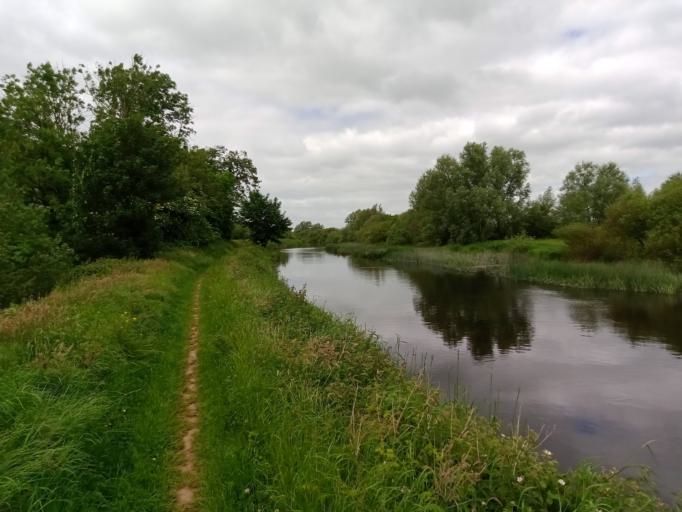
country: IE
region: Leinster
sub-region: County Carlow
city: Carlow
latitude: 52.8009
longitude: -6.9636
